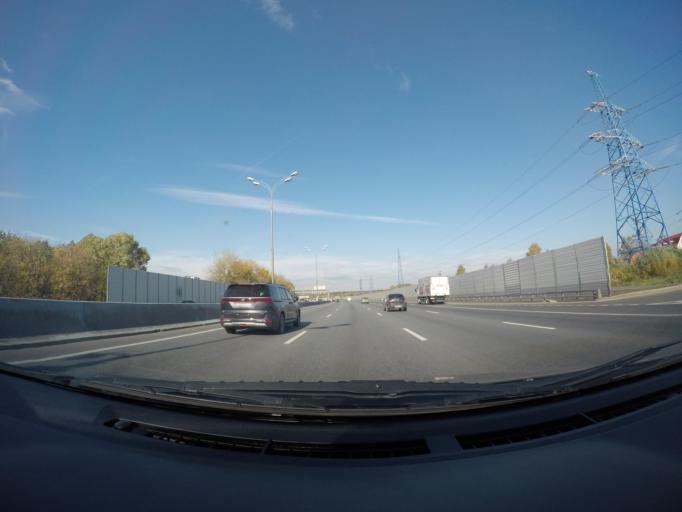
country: RU
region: Moscow
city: Gol'yanovo
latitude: 55.8199
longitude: 37.8379
